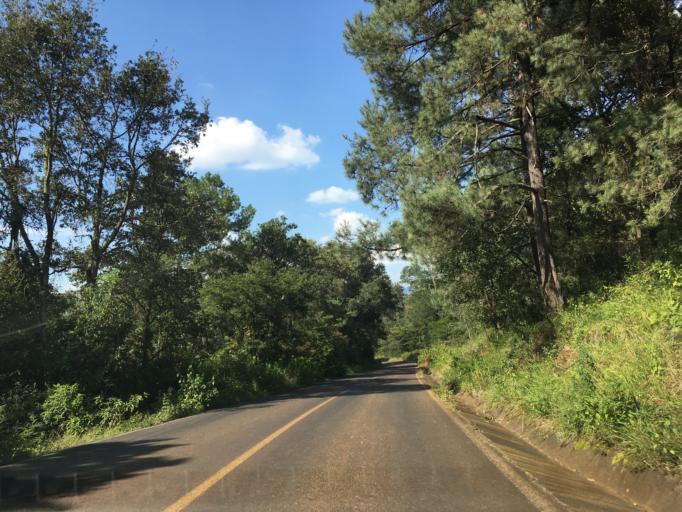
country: MX
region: Michoacan
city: Acuitzio del Canje
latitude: 19.5421
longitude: -101.2584
